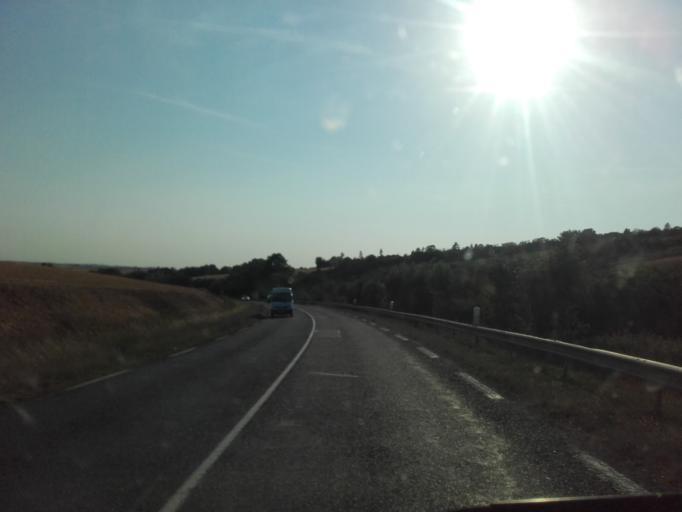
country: FR
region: Bourgogne
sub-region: Departement de l'Yonne
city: Venoy
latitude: 47.7955
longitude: 3.6392
